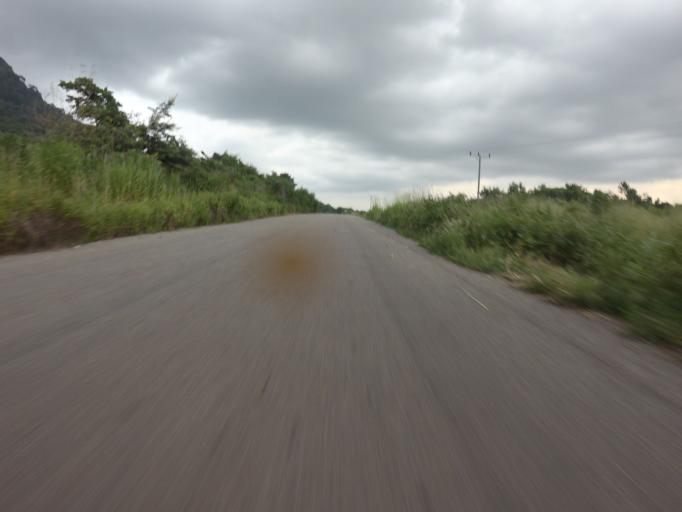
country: GH
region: Volta
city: Kpandu
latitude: 6.7930
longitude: 0.3705
